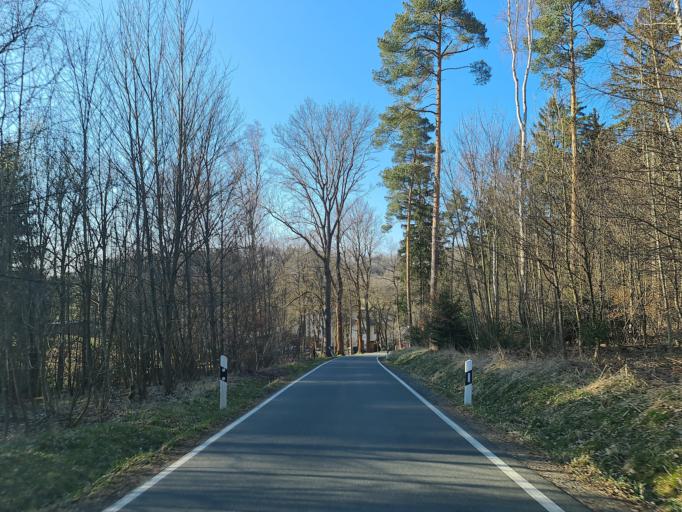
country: DE
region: Saxony
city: Pohl
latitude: 50.5375
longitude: 12.1569
